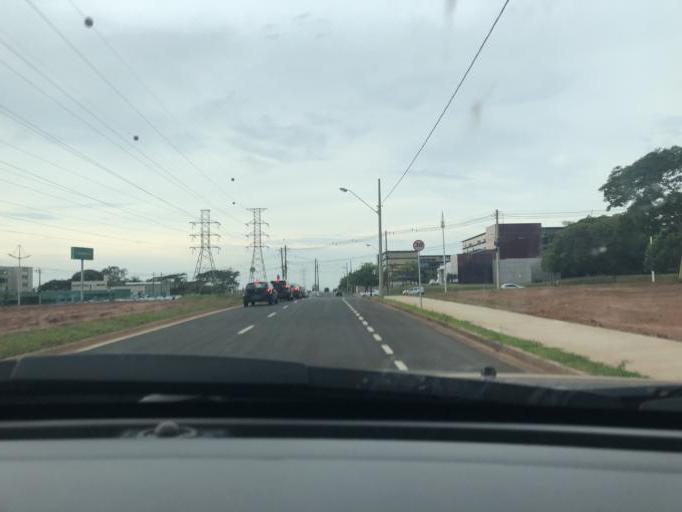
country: BR
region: Sao Paulo
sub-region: Sao Jose Do Rio Preto
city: Sao Jose do Rio Preto
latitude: -20.8446
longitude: -49.4039
